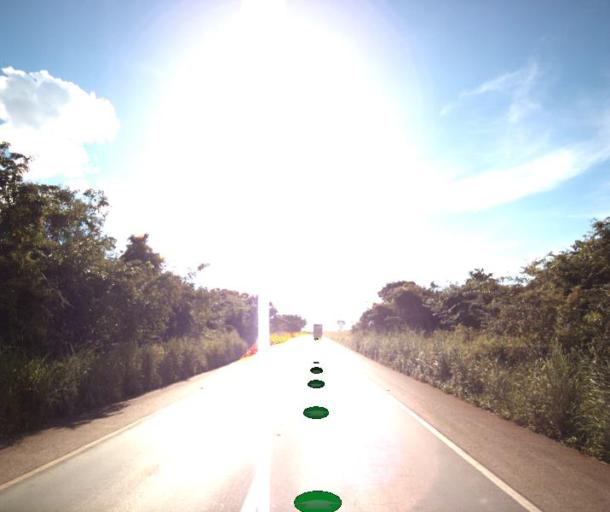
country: BR
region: Goias
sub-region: Rialma
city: Rialma
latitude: -15.3976
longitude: -49.5405
